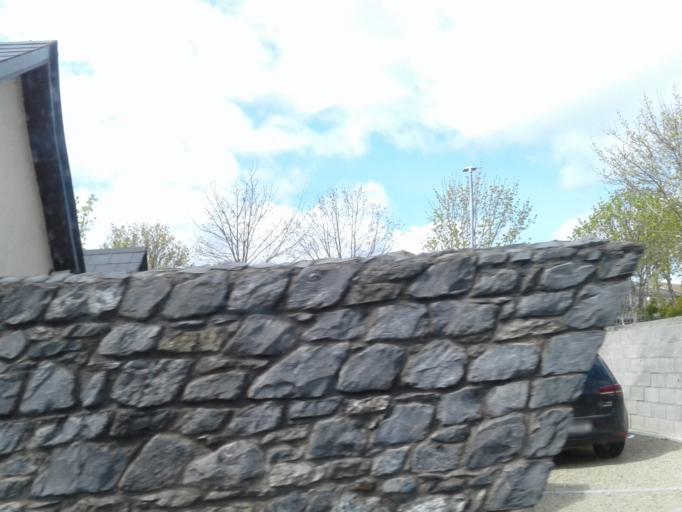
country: IE
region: Leinster
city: Malahide
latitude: 53.4541
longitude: -6.1766
